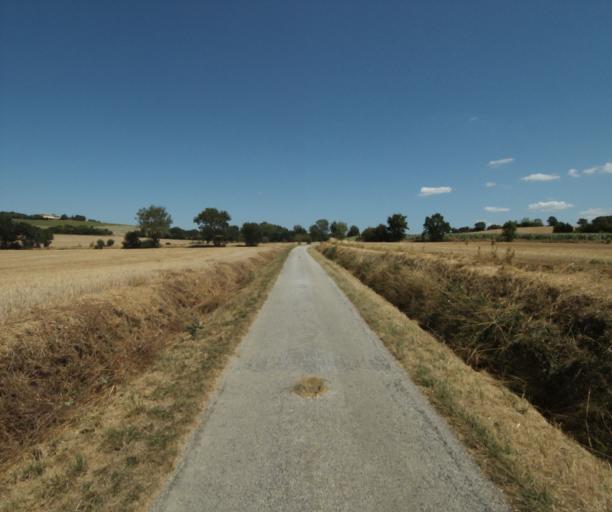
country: FR
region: Midi-Pyrenees
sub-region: Departement de la Haute-Garonne
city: Saint-Felix-Lauragais
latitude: 43.4836
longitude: 1.8928
